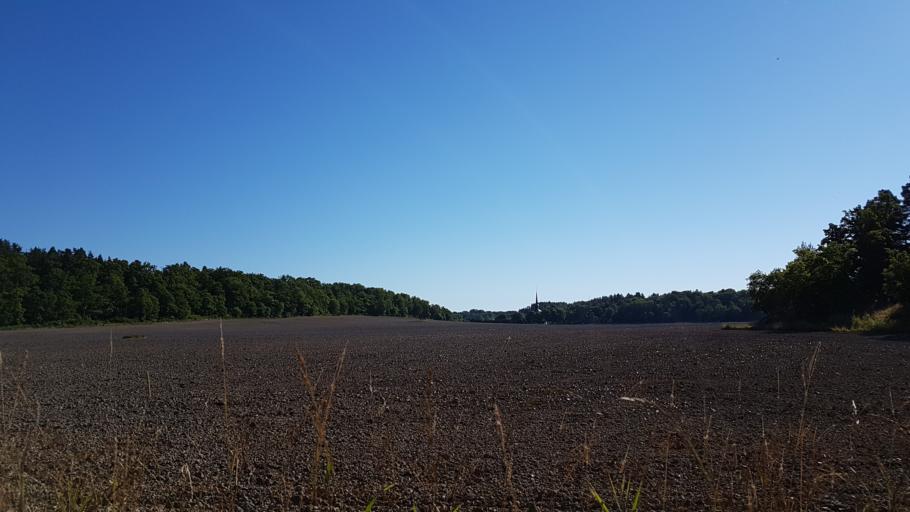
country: SE
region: OEstergoetland
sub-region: Valdemarsviks Kommun
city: Gusum
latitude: 58.4288
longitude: 16.5763
